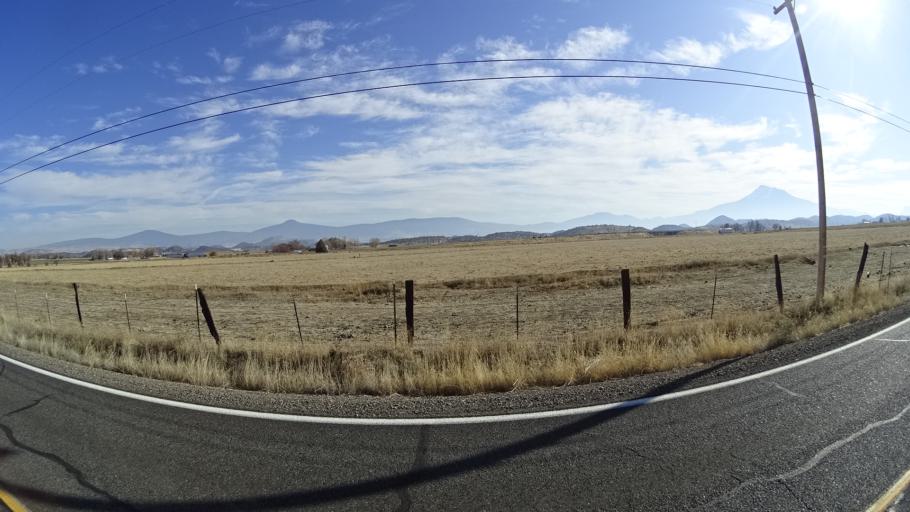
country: US
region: California
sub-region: Siskiyou County
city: Montague
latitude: 41.6305
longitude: -122.5297
